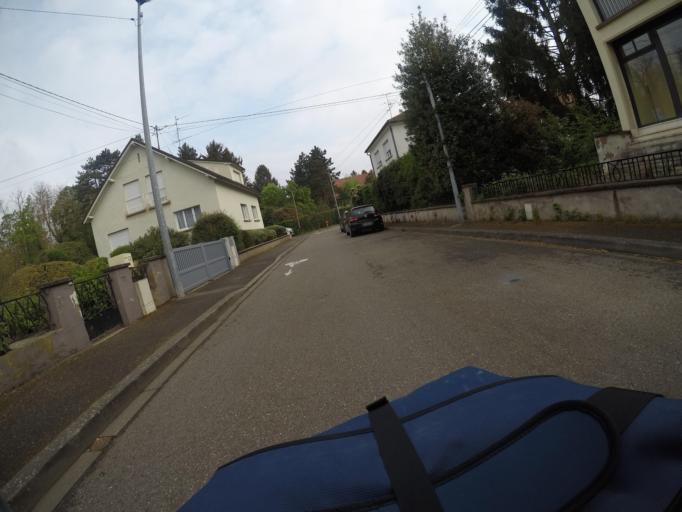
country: FR
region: Alsace
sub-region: Departement du Bas-Rhin
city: Wolfisheim
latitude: 48.5880
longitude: 7.6645
